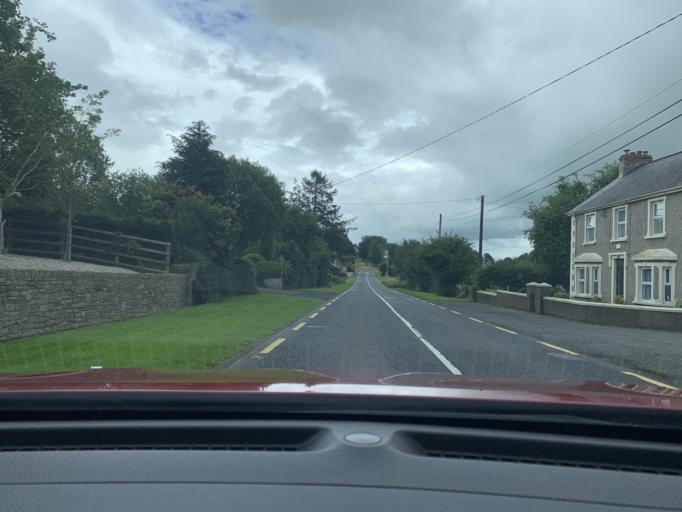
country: IE
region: Ulster
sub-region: County Donegal
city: Raphoe
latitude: 54.8023
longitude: -7.6154
